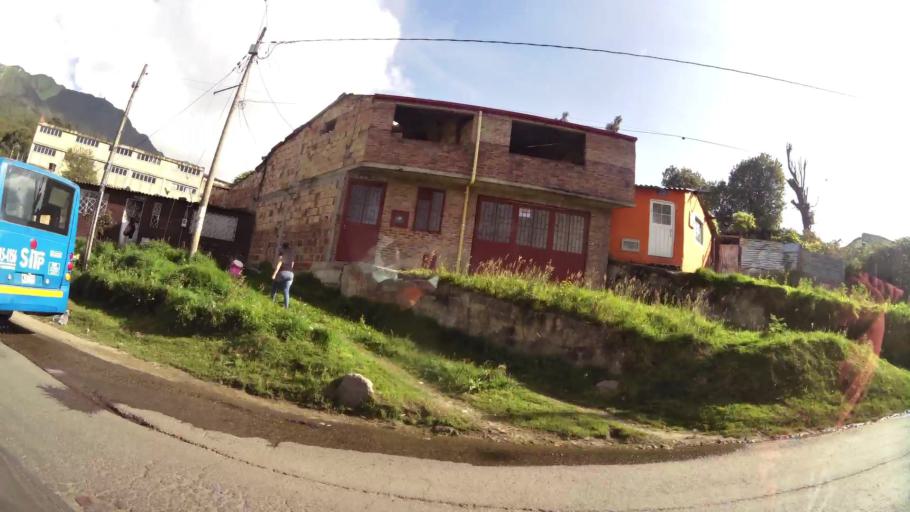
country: CO
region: Bogota D.C.
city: Bogota
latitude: 4.5324
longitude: -74.0857
